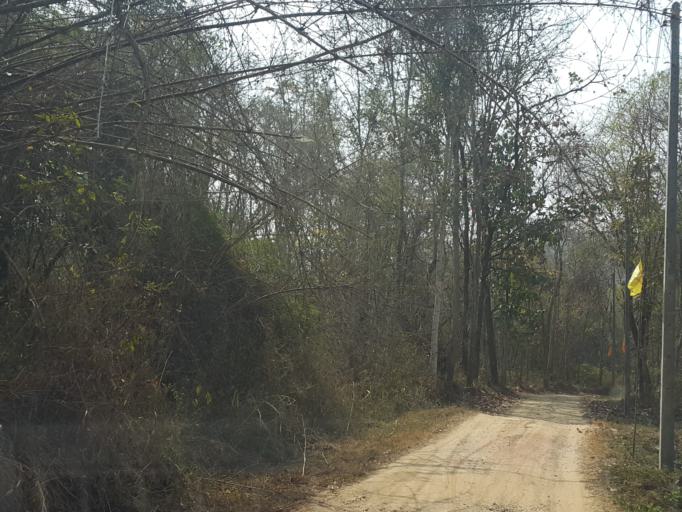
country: TH
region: Chiang Mai
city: Hang Dong
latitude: 18.7128
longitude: 98.8533
